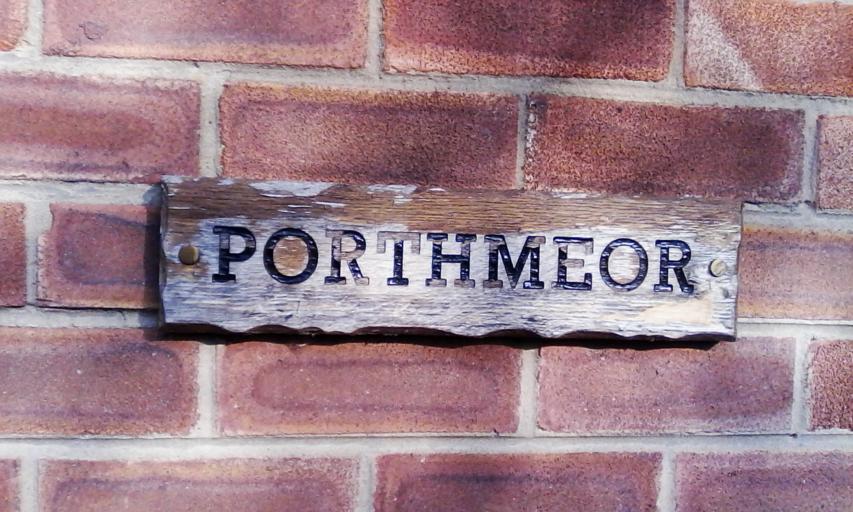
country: GB
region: England
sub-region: Nottinghamshire
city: Burton Joyce
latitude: 52.9768
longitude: -1.0819
